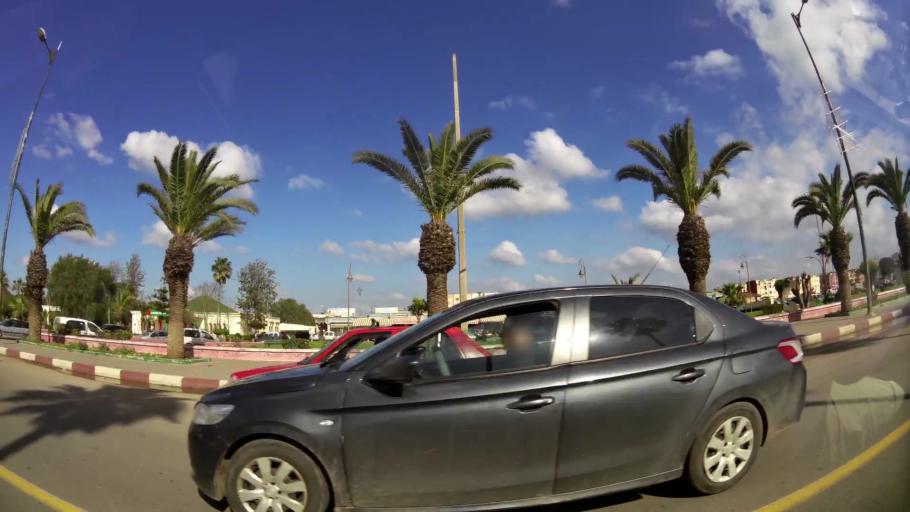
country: MA
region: Chaouia-Ouardigha
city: Nouaseur
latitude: 33.3737
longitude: -7.5418
